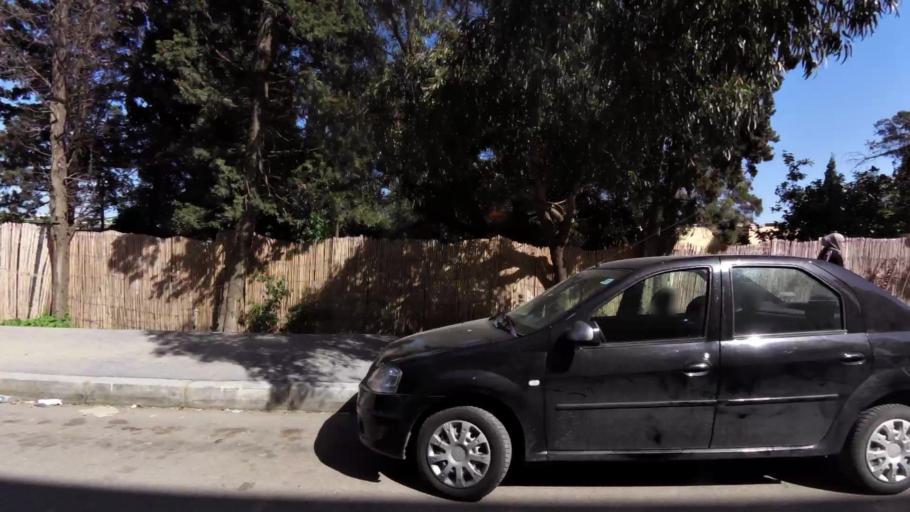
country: MA
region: Tanger-Tetouan
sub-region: Tanger-Assilah
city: Tangier
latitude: 35.7499
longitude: -5.8071
